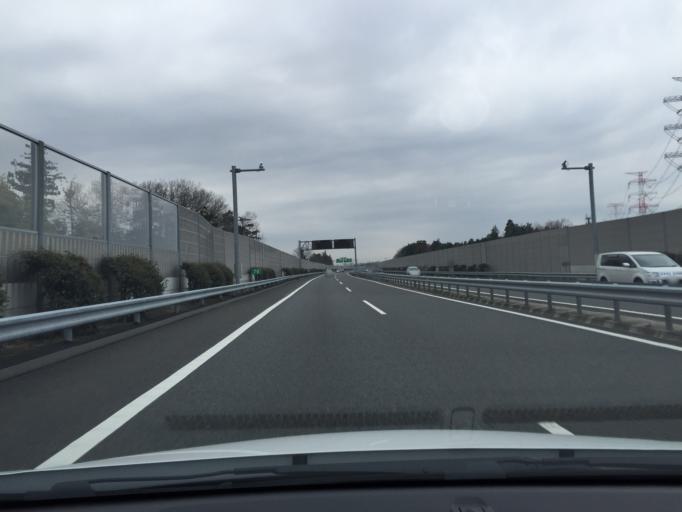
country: JP
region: Saitama
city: Sakado
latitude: 35.9412
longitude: 139.4116
